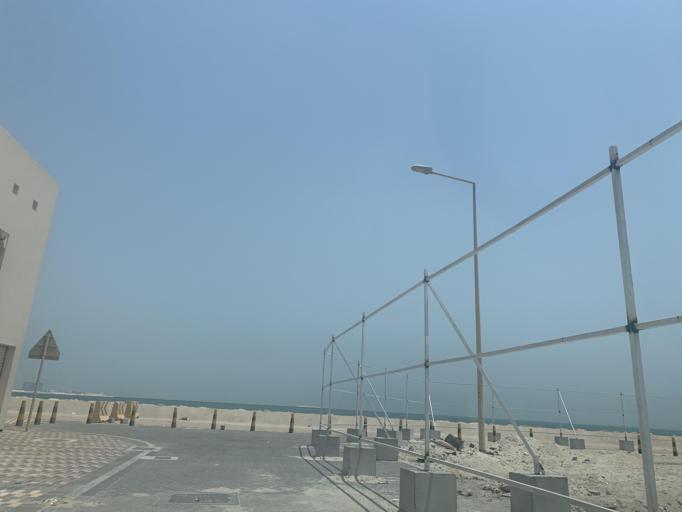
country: BH
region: Muharraq
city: Al Hadd
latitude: 26.2415
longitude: 50.6719
